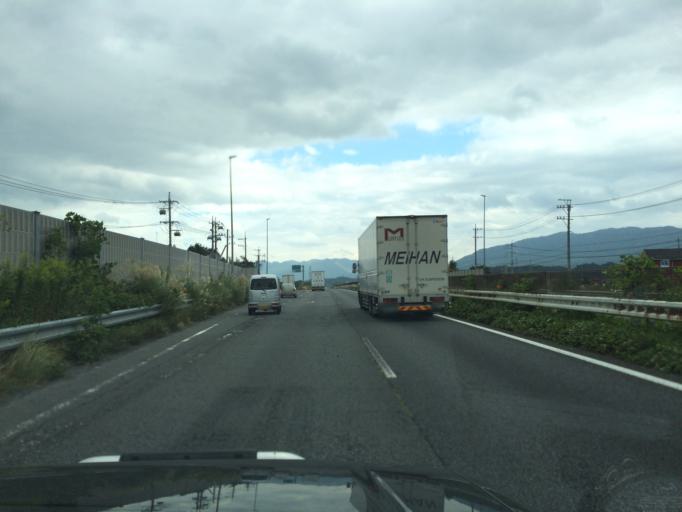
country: JP
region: Mie
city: Ueno-ebisumachi
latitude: 34.8030
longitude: 136.1875
